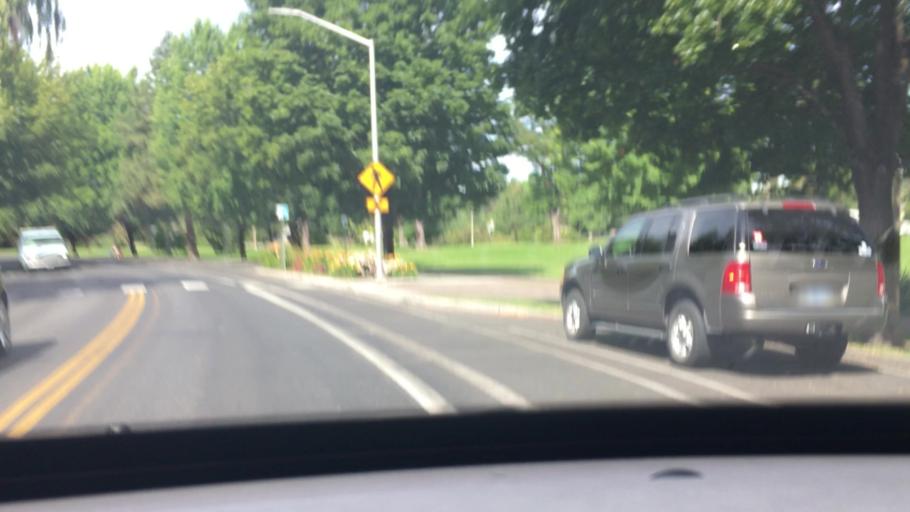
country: US
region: Oregon
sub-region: Deschutes County
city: Bend
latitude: 44.0591
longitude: -121.3203
